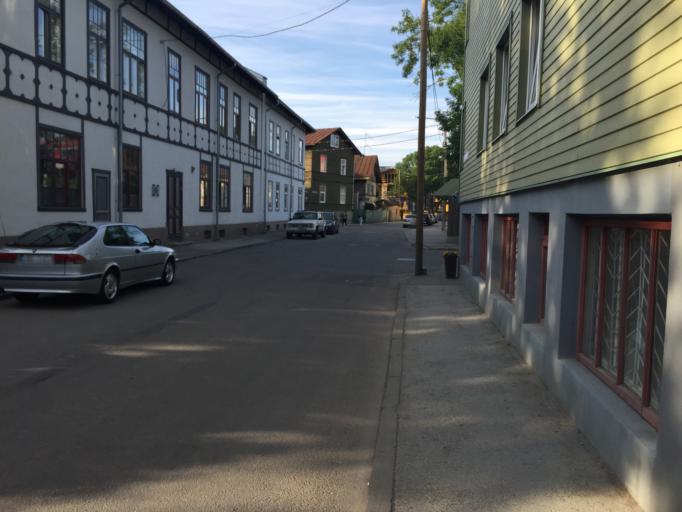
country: EE
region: Harju
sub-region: Tallinna linn
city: Tallinn
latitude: 59.4467
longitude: 24.7396
